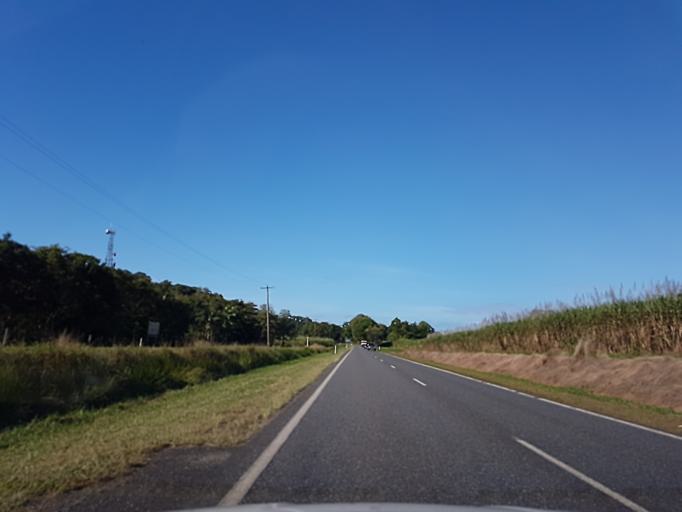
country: AU
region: Queensland
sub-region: Cairns
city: Port Douglas
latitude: -16.4362
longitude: 145.3822
